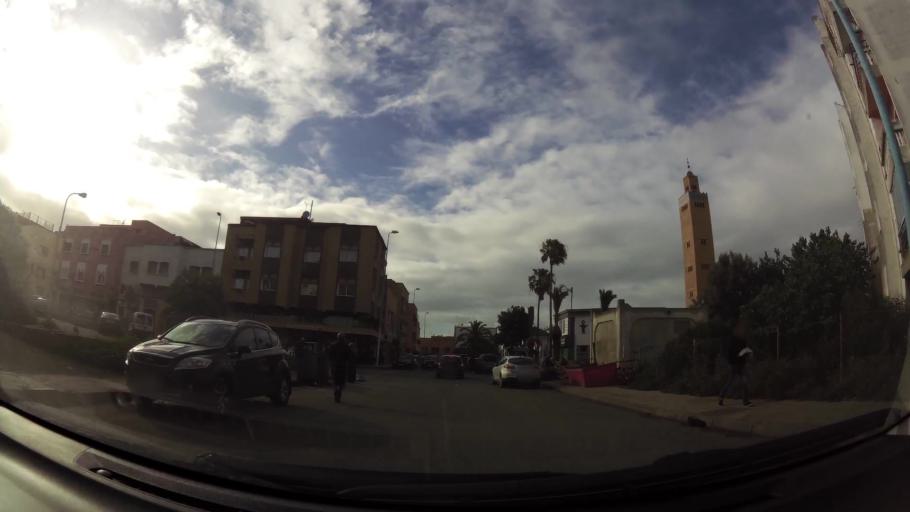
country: MA
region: Doukkala-Abda
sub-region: El-Jadida
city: El Jadida
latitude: 33.2425
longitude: -8.5251
